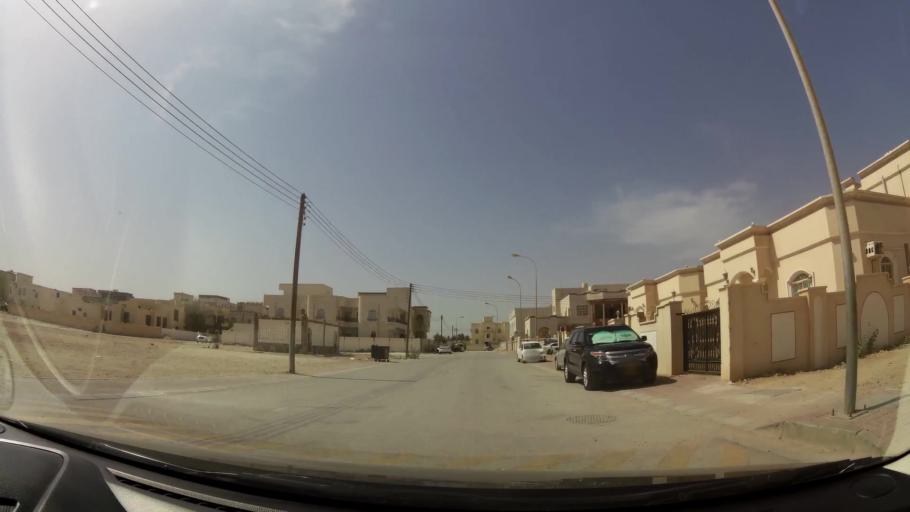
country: OM
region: Zufar
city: Salalah
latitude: 17.0483
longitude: 54.1583
